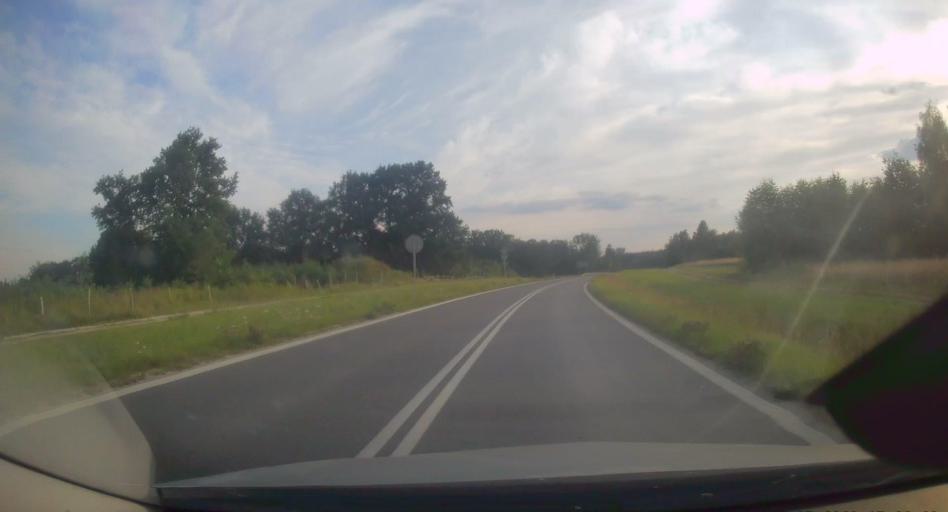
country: PL
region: Lesser Poland Voivodeship
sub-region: Powiat brzeski
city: Przyborow
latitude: 50.0229
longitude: 20.6288
